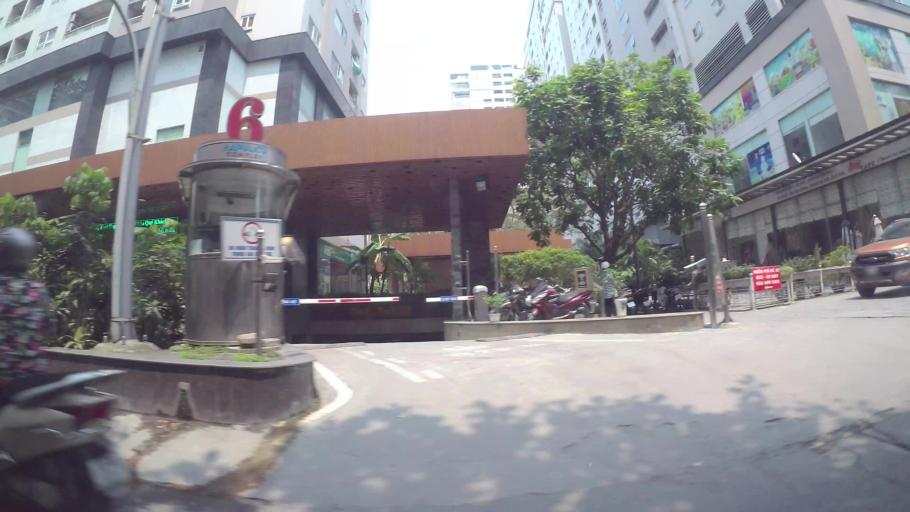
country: VN
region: Ha Noi
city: Thanh Xuan
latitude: 20.9998
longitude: 105.8076
